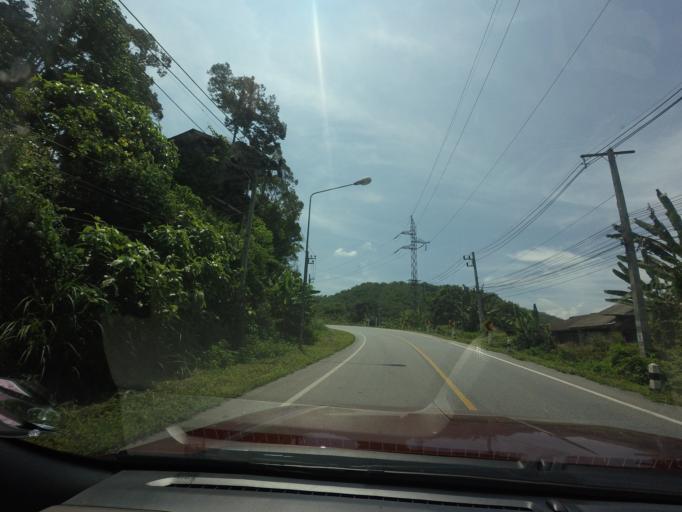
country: TH
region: Yala
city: Betong
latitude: 5.8236
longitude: 101.1118
